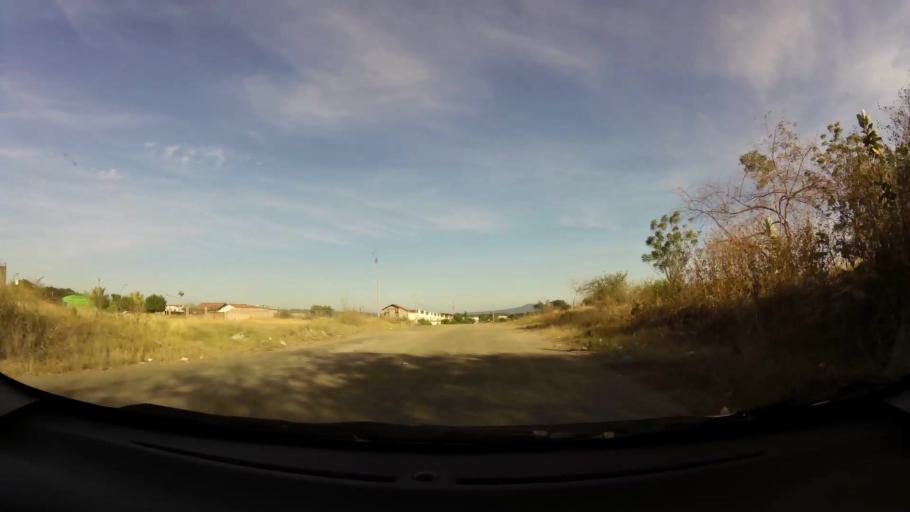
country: SV
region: San Miguel
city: San Miguel
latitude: 13.4580
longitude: -88.1721
